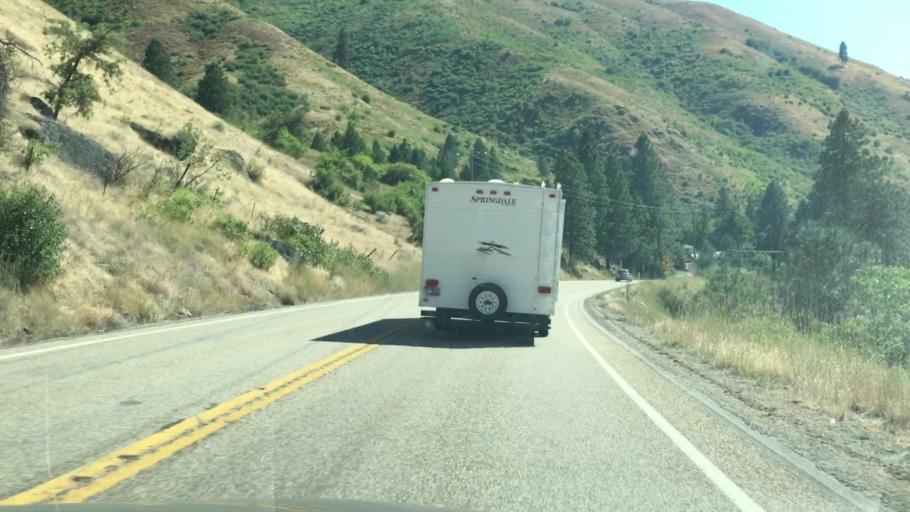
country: US
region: Idaho
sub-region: Boise County
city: Idaho City
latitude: 44.0294
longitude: -116.1344
